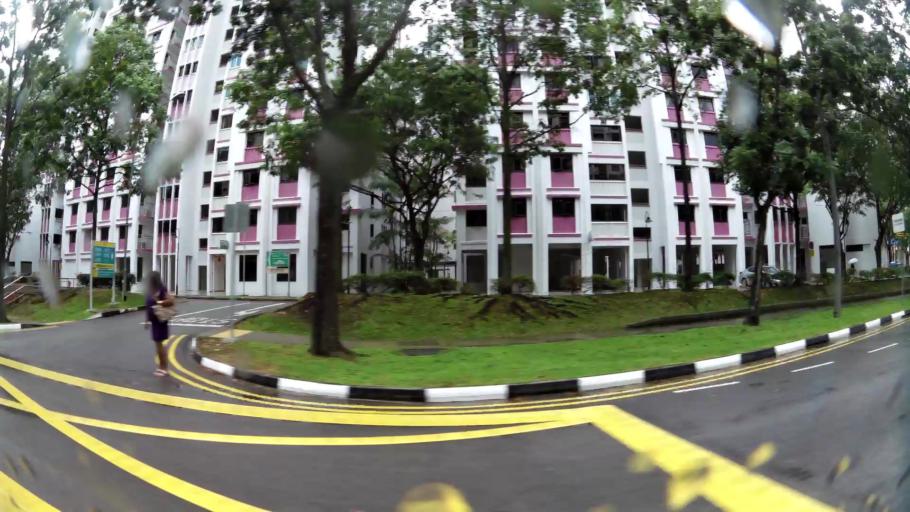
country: MY
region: Johor
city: Kampung Pasir Gudang Baru
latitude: 1.3877
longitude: 103.8972
